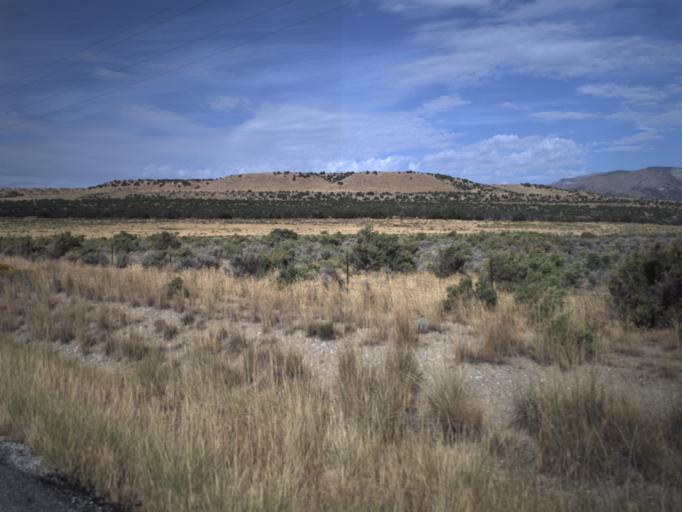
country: US
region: Idaho
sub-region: Minidoka County
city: Heyburn
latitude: 41.8211
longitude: -113.1924
